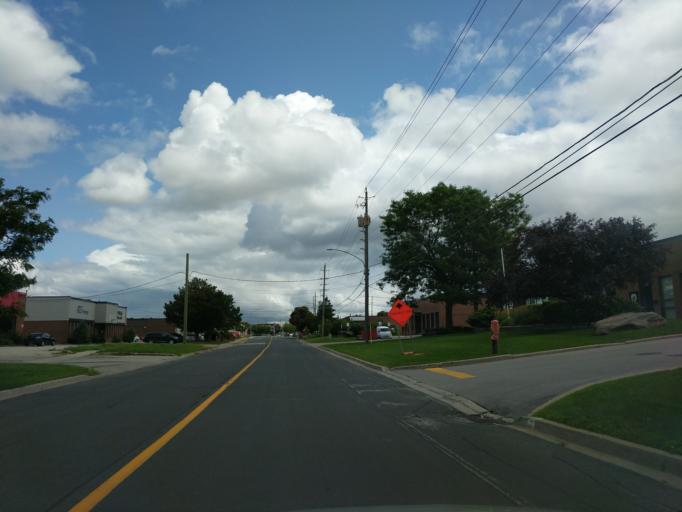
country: CA
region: Ontario
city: Willowdale
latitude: 43.8214
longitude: -79.3539
